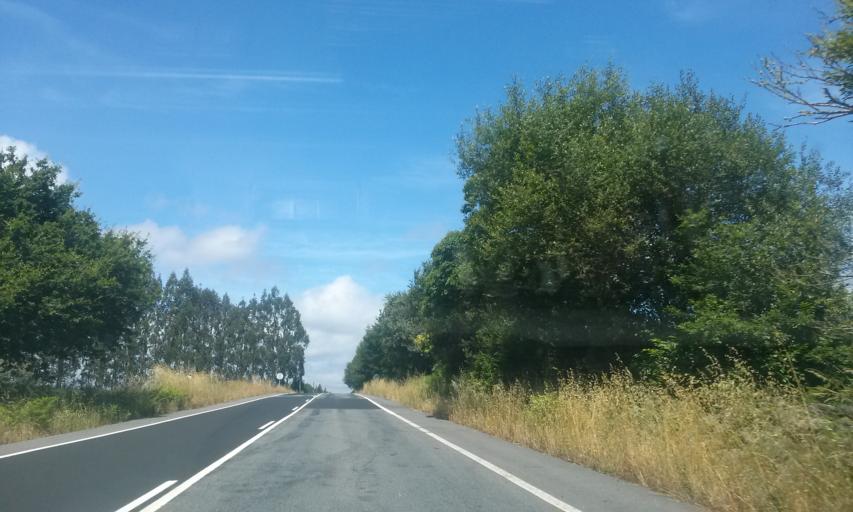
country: ES
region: Galicia
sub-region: Provincia de Lugo
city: Outeiro de Rei
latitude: 43.0200
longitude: -7.6757
